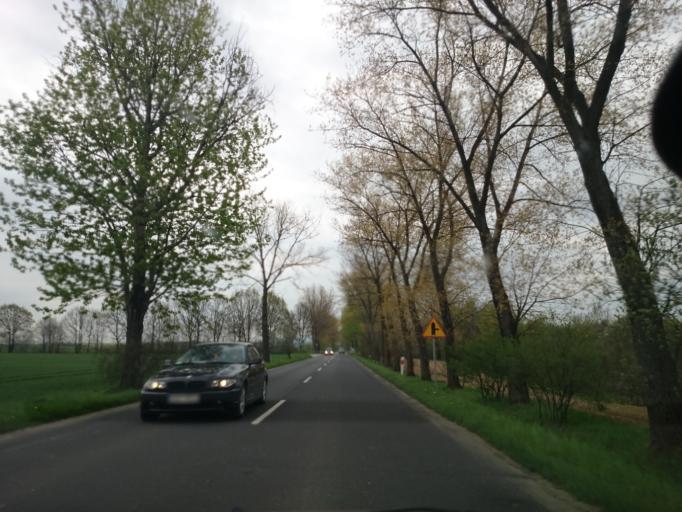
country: PL
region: Opole Voivodeship
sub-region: Powiat nyski
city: Glucholazy
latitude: 50.3578
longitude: 17.3781
